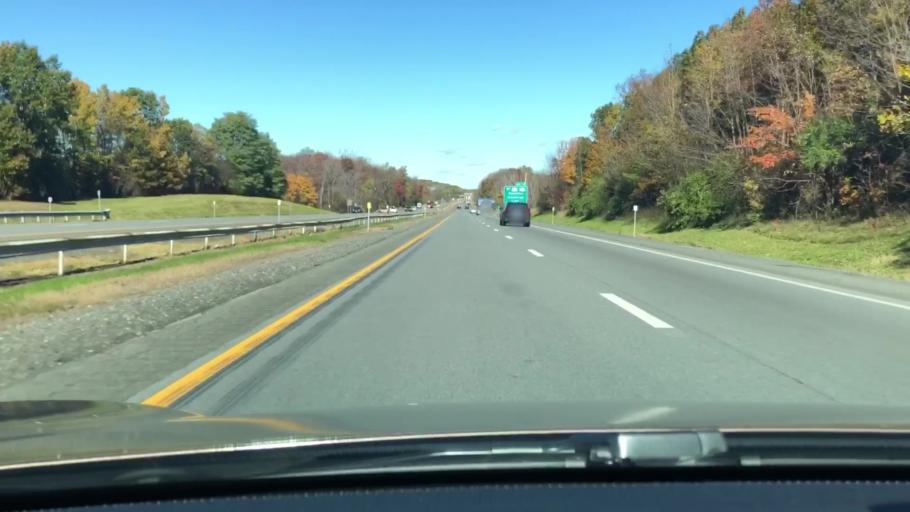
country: US
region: New York
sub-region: Orange County
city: Gardnertown
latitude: 41.4928
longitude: -74.0783
